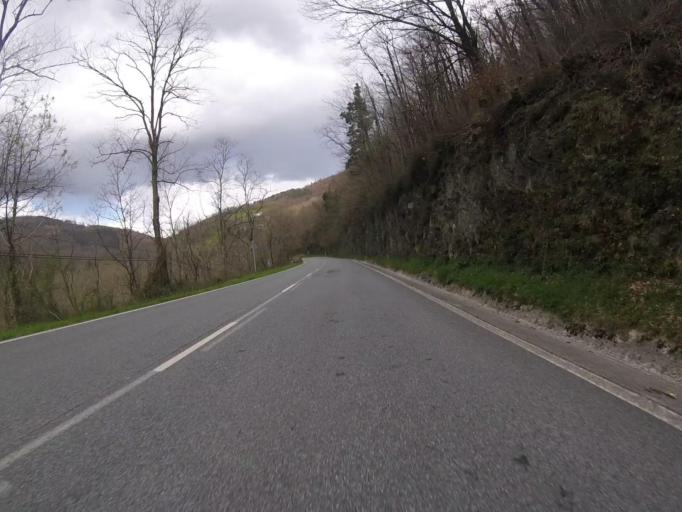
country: ES
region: Navarre
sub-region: Provincia de Navarra
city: Etxalar
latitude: 43.2367
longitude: -1.6605
